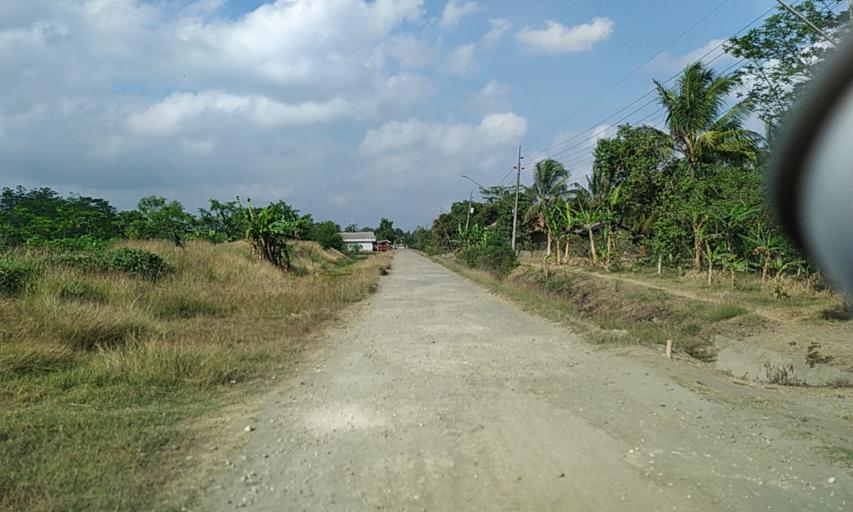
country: ID
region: Central Java
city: Sidakaya
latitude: -7.6169
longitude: 108.8591
